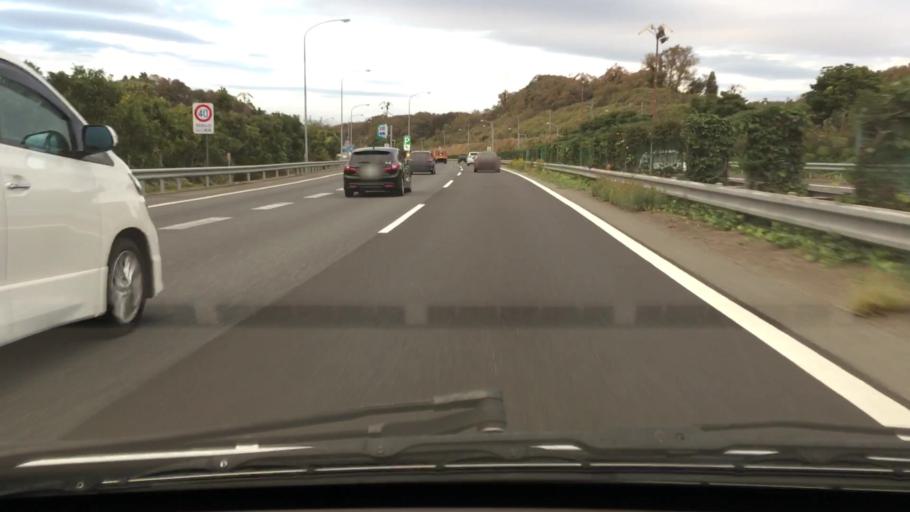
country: JP
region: Chiba
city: Ichihara
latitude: 35.4581
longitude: 140.0848
